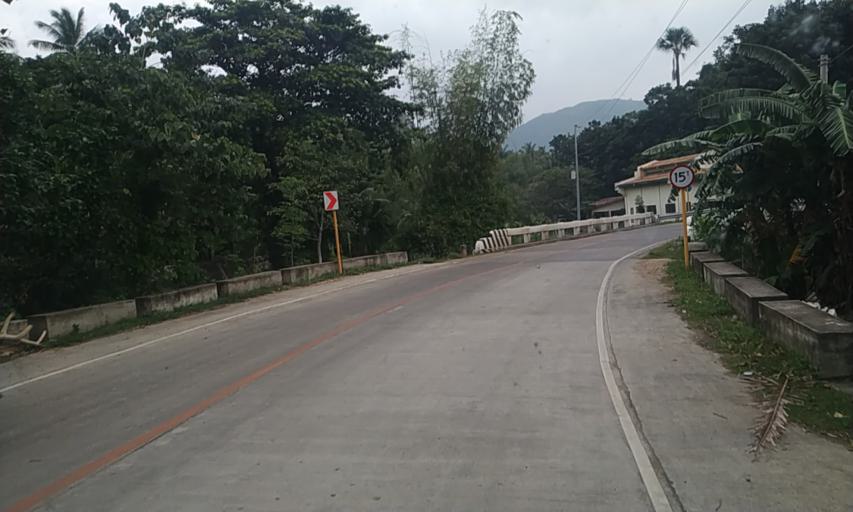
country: PH
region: Central Visayas
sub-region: Province of Negros Oriental
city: Calamba
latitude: 10.1960
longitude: 123.2943
